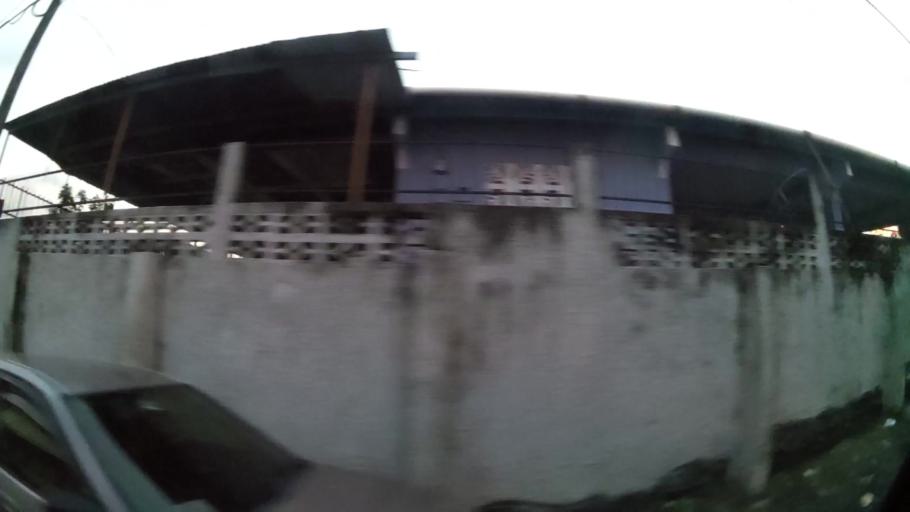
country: PA
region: Panama
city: Tocumen
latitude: 9.0820
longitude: -79.3967
